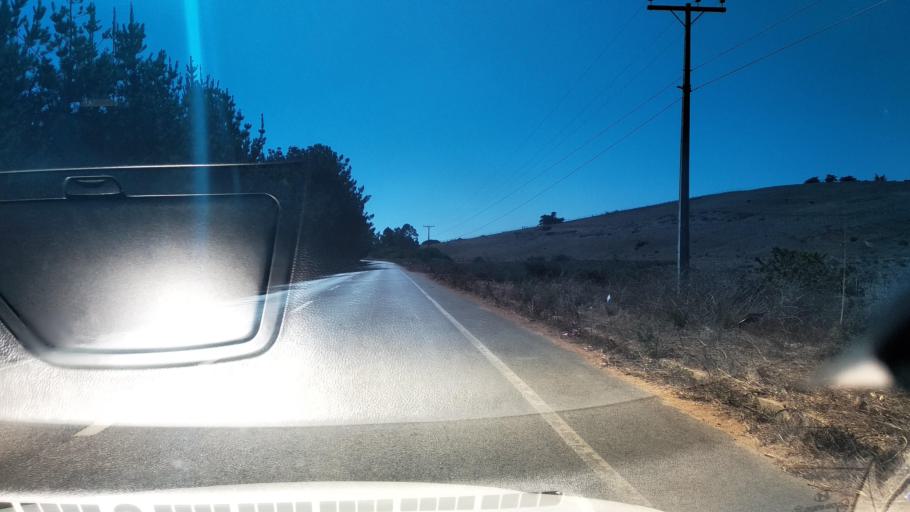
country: CL
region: O'Higgins
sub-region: Provincia de Colchagua
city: Santa Cruz
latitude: -34.4608
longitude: -72.0244
